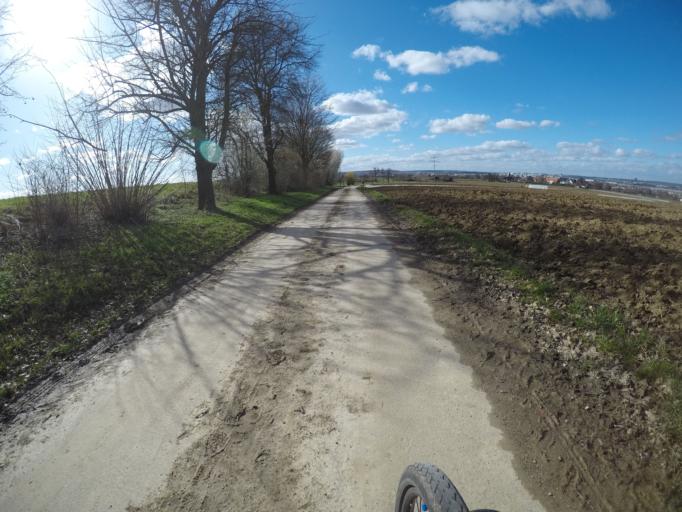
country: DE
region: Baden-Wuerttemberg
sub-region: Regierungsbezirk Stuttgart
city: Filderstadt
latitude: 48.6619
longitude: 9.2433
